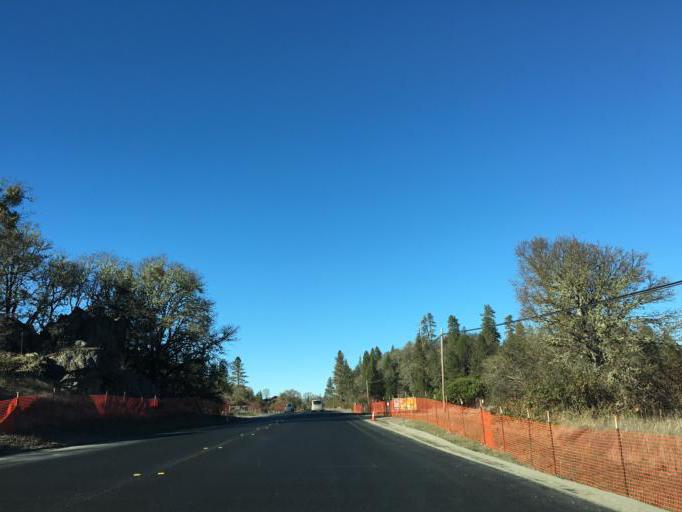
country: US
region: California
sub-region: Mendocino County
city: Laytonville
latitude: 39.6345
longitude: -123.4682
